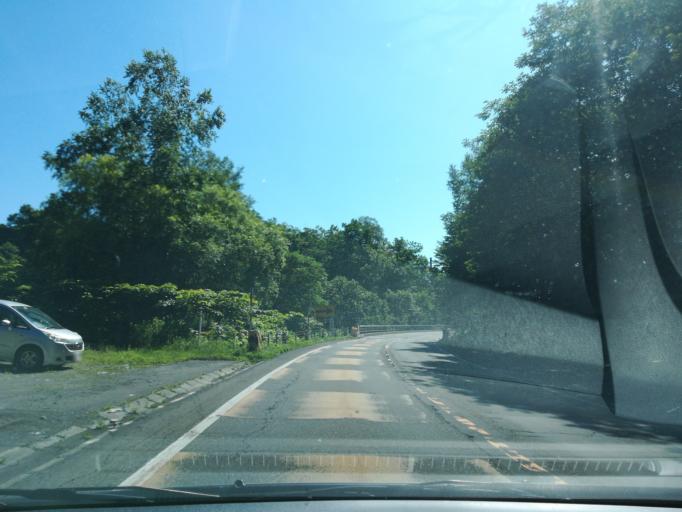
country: JP
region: Hokkaido
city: Chitose
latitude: 42.9108
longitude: 141.9459
